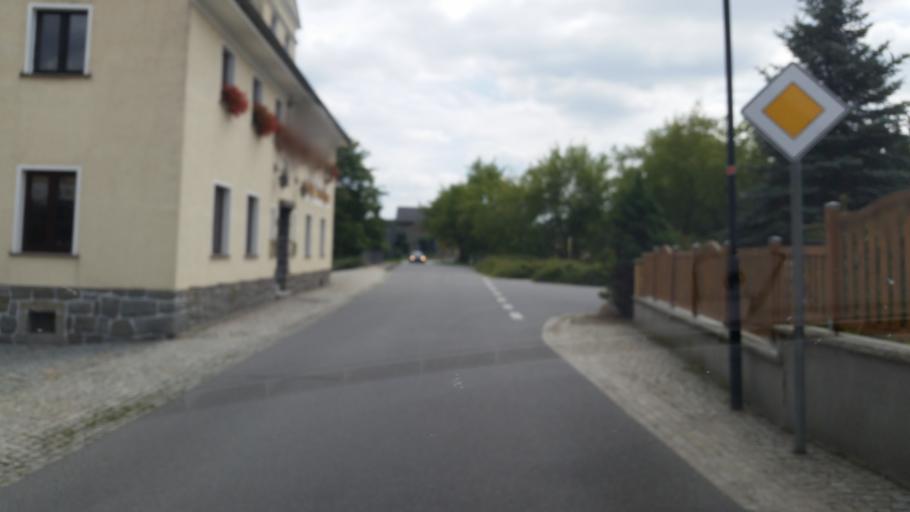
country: DE
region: Saxony
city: Puschwitz
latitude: 51.2213
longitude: 14.3130
